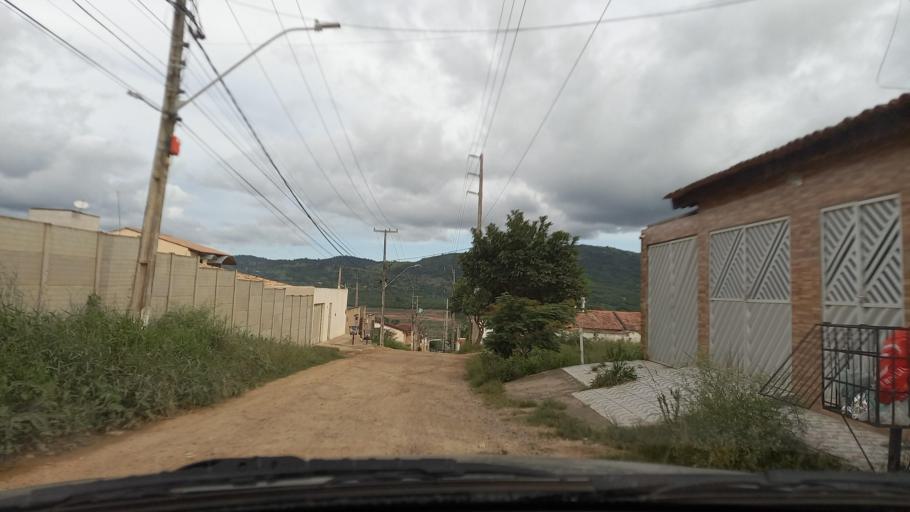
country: BR
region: Pernambuco
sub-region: Gravata
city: Gravata
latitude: -8.2166
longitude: -35.5726
